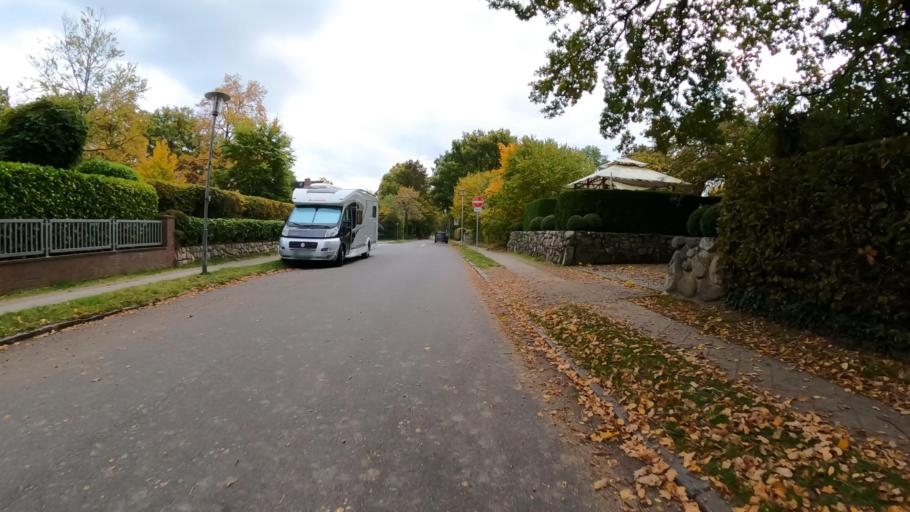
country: DE
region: Schleswig-Holstein
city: Ahrensburg
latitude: 53.6651
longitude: 10.2430
